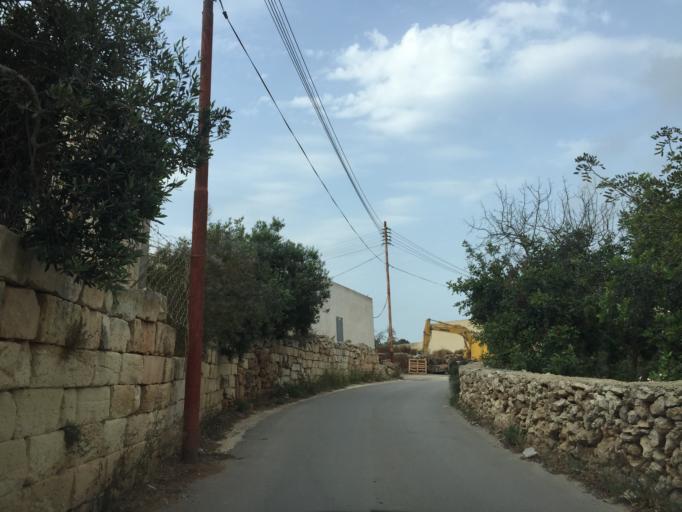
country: MT
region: L-Imgarr
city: Imgarr
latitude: 35.9297
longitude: 14.3834
